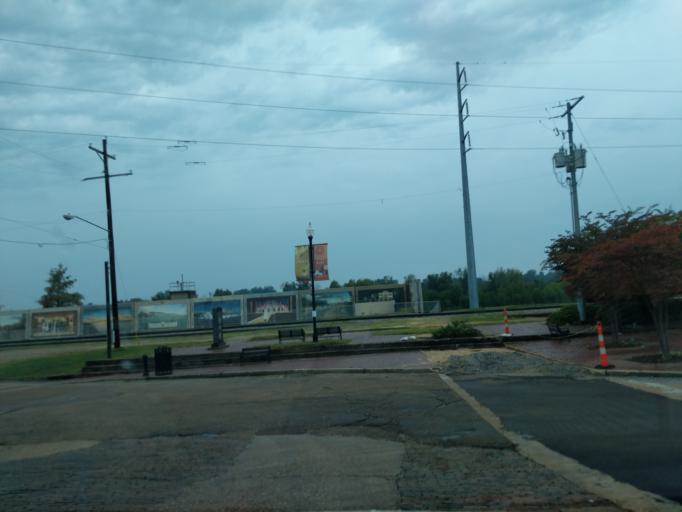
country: US
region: Mississippi
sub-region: Warren County
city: Vicksburg
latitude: 32.3522
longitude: -90.8827
